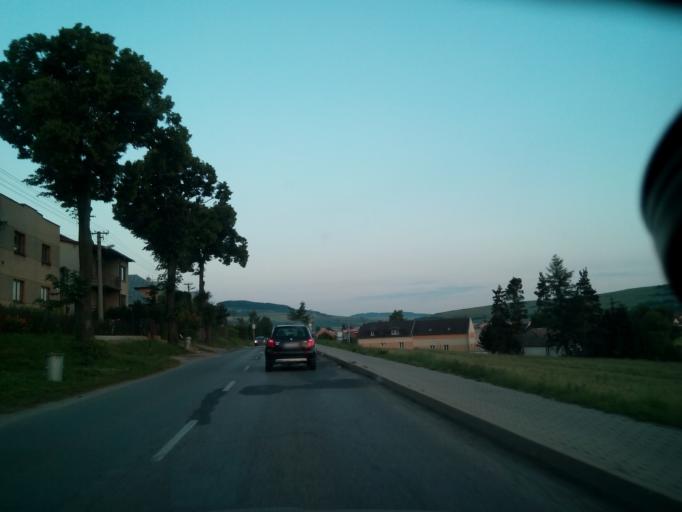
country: SK
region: Presovsky
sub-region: Okres Presov
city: Kezmarok
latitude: 49.1267
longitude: 20.4373
